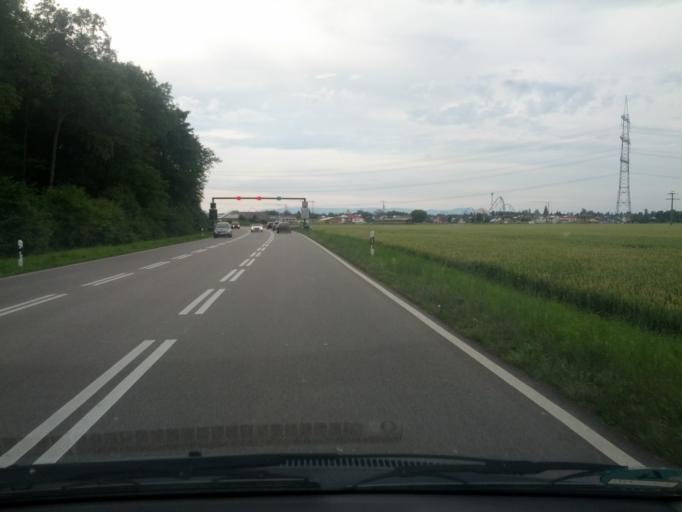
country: DE
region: Baden-Wuerttemberg
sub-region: Freiburg Region
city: Rust
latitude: 48.2581
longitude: 7.7380
